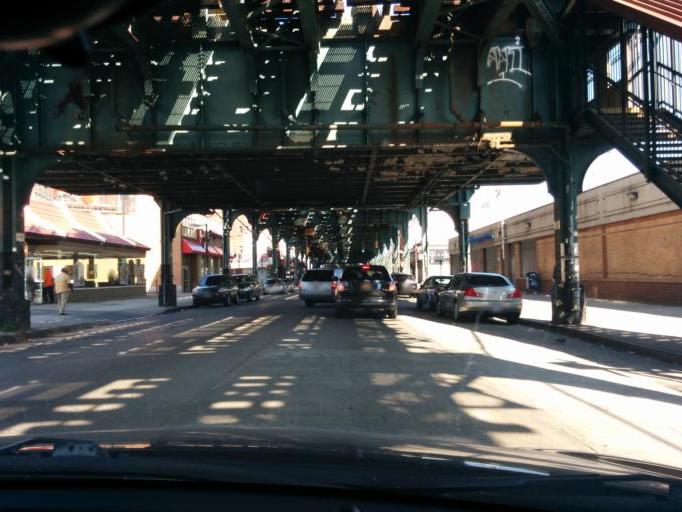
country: US
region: New York
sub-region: Kings County
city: East New York
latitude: 40.6890
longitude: -73.9212
